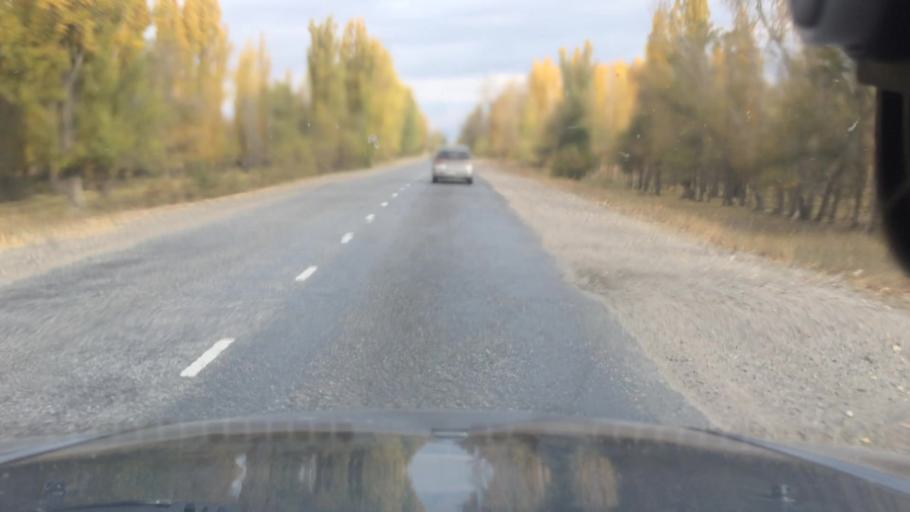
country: KG
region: Ysyk-Koel
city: Tyup
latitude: 42.6128
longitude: 78.3664
